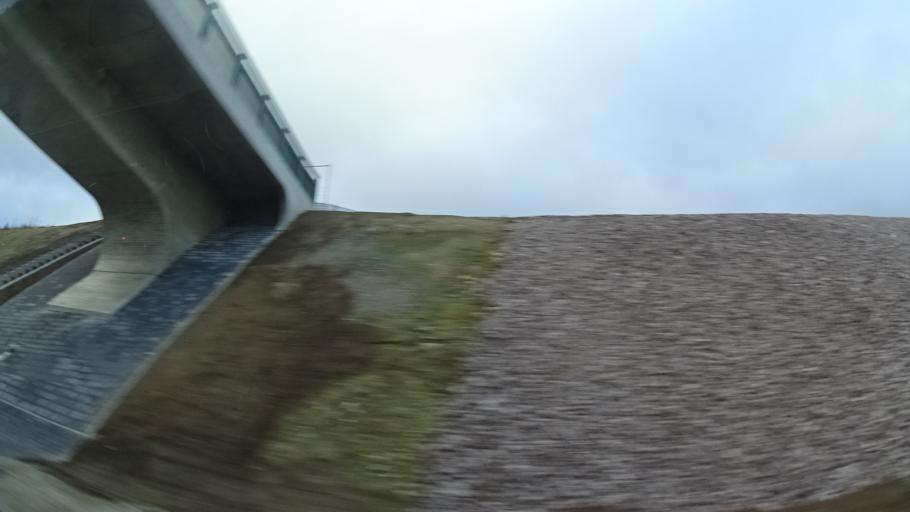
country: DE
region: Thuringia
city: Stadtilm
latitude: 50.7583
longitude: 11.0612
